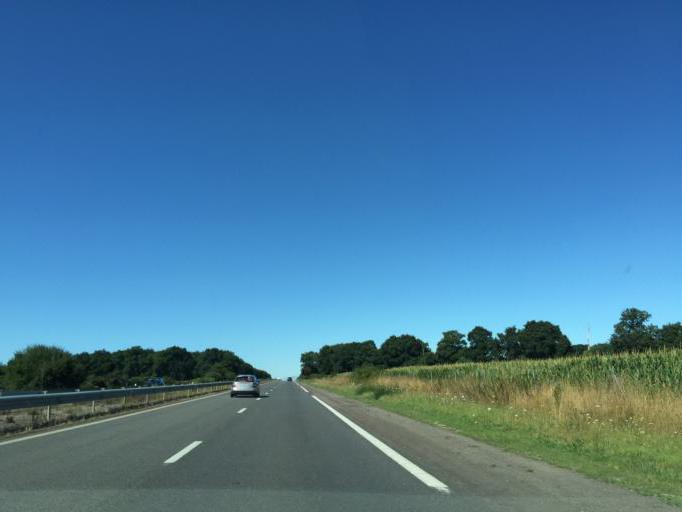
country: FR
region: Brittany
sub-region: Departement des Cotes-d'Armor
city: Plelan-le-Petit
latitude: 48.4227
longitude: -2.2547
